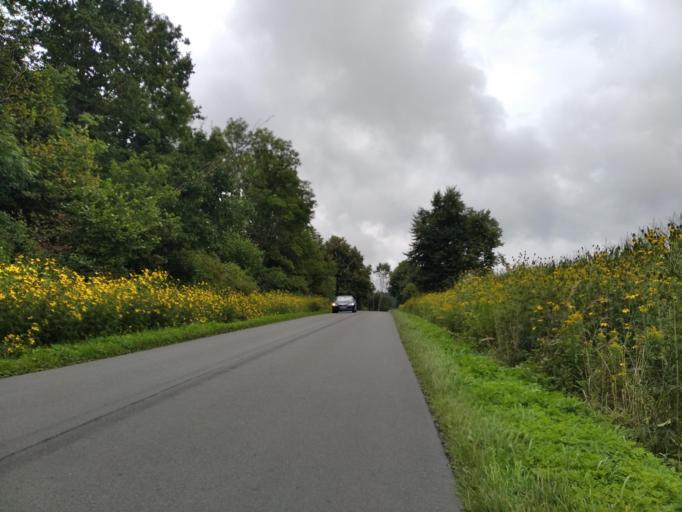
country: PL
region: Subcarpathian Voivodeship
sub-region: Powiat brzozowski
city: Nozdrzec
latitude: 49.7256
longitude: 22.2856
